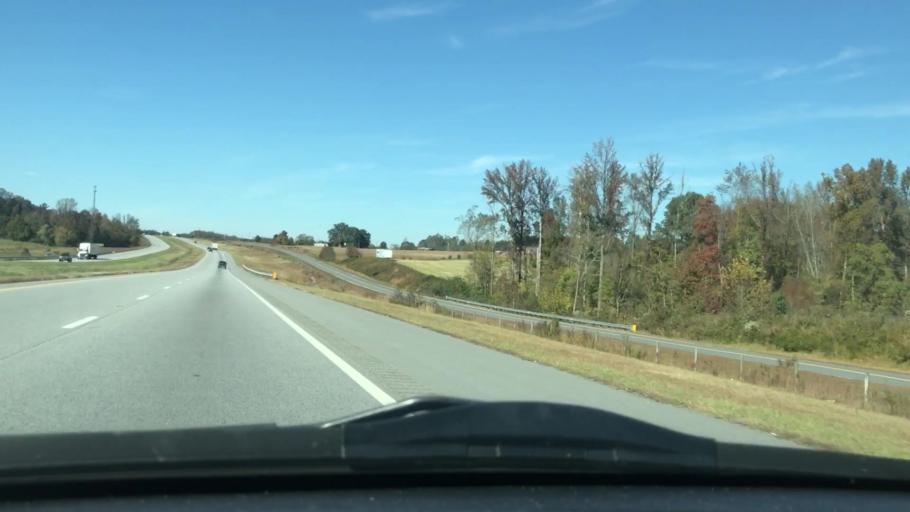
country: US
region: North Carolina
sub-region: Randolph County
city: Randleman
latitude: 35.8623
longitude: -79.8883
